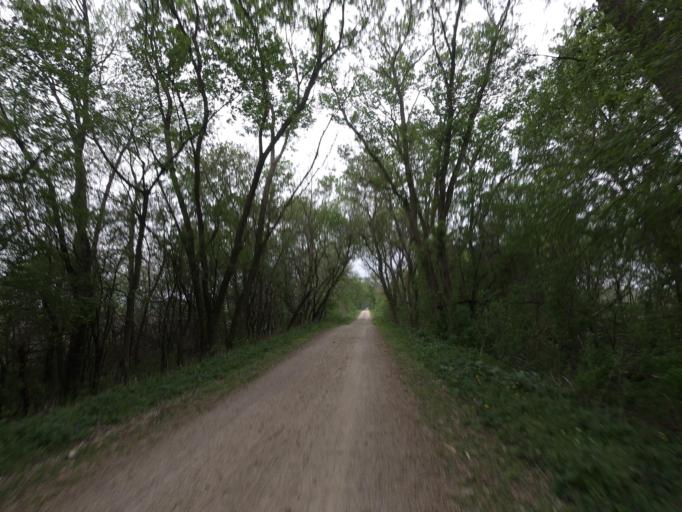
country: US
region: Wisconsin
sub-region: Jefferson County
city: Lake Mills
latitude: 43.0631
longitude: -88.8972
